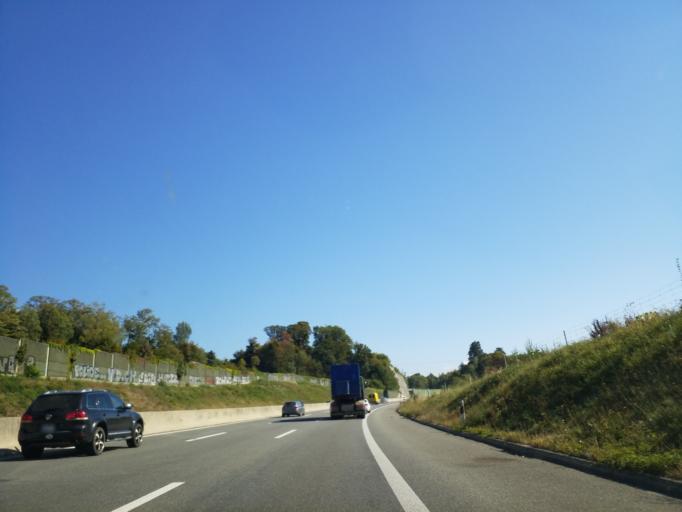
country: CH
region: Vaud
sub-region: Lausanne District
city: Romanel
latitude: 46.5590
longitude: 6.5951
